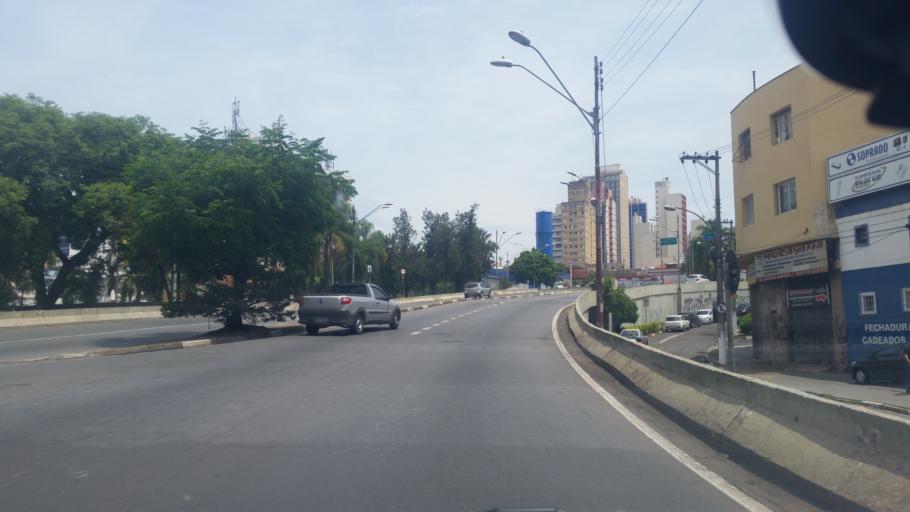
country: BR
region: Sao Paulo
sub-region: Campinas
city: Campinas
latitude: -22.9024
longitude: -47.0643
